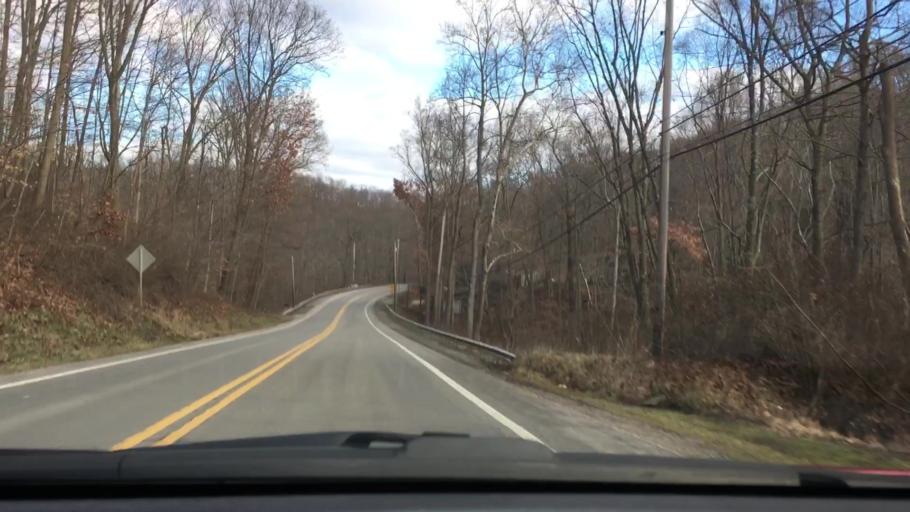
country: US
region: Pennsylvania
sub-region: Westmoreland County
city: Avonmore
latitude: 40.6239
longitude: -79.4293
